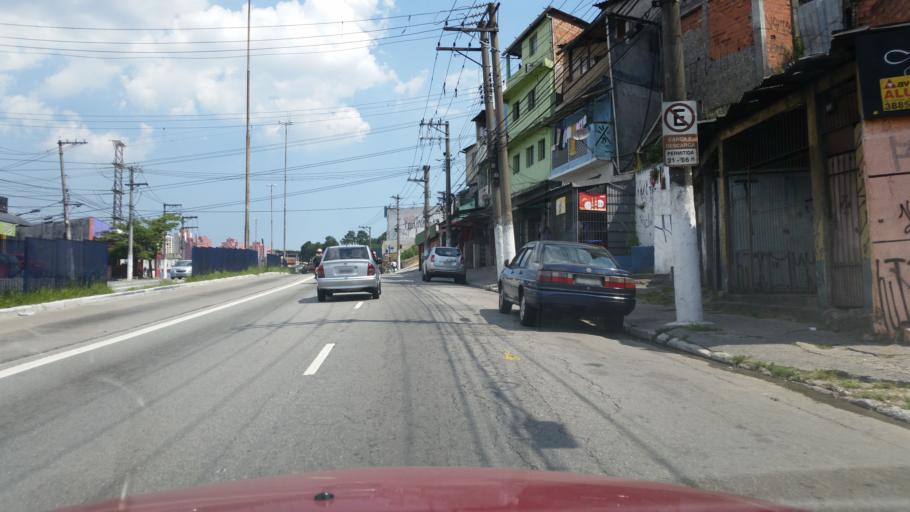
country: BR
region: Sao Paulo
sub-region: Diadema
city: Diadema
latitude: -23.6774
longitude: -46.6416
